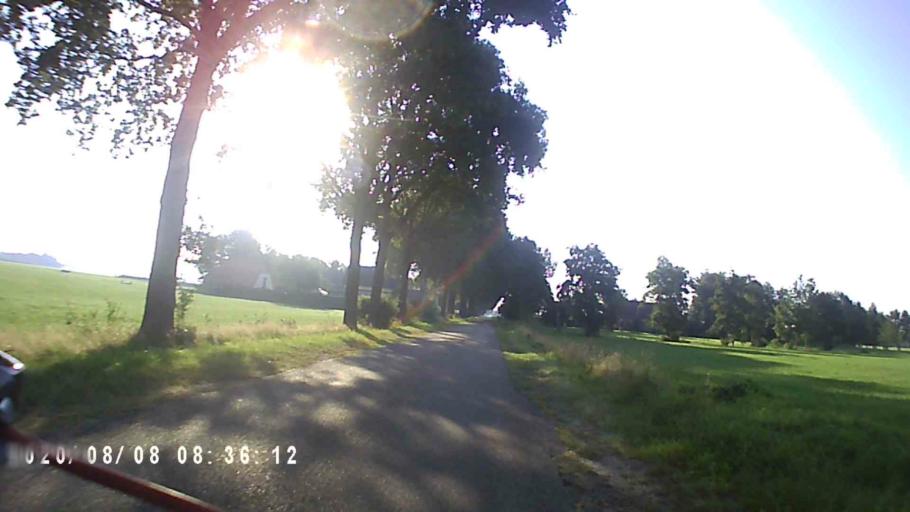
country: NL
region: Groningen
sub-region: Gemeente Leek
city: Leek
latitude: 53.0750
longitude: 6.3343
